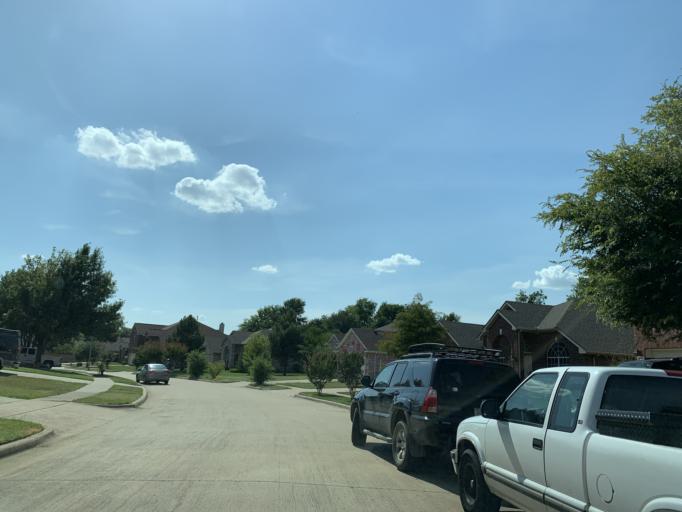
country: US
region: Texas
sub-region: Dallas County
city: Cedar Hill
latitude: 32.6528
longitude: -97.0084
